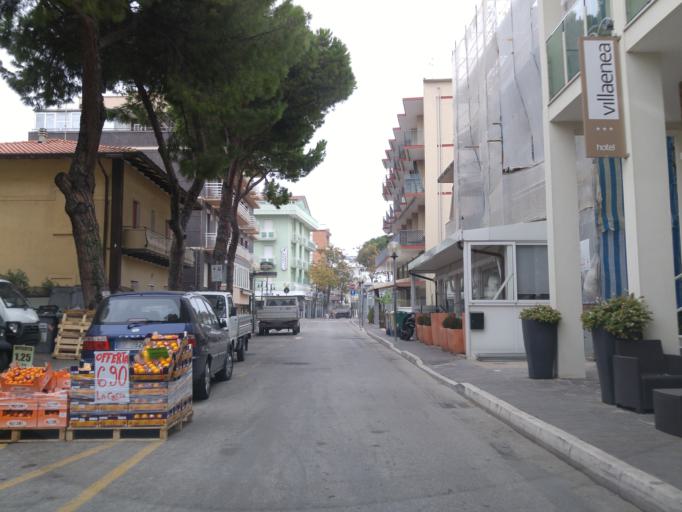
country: IT
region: Emilia-Romagna
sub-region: Provincia di Rimini
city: Cattolica
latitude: 43.9658
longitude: 12.7347
